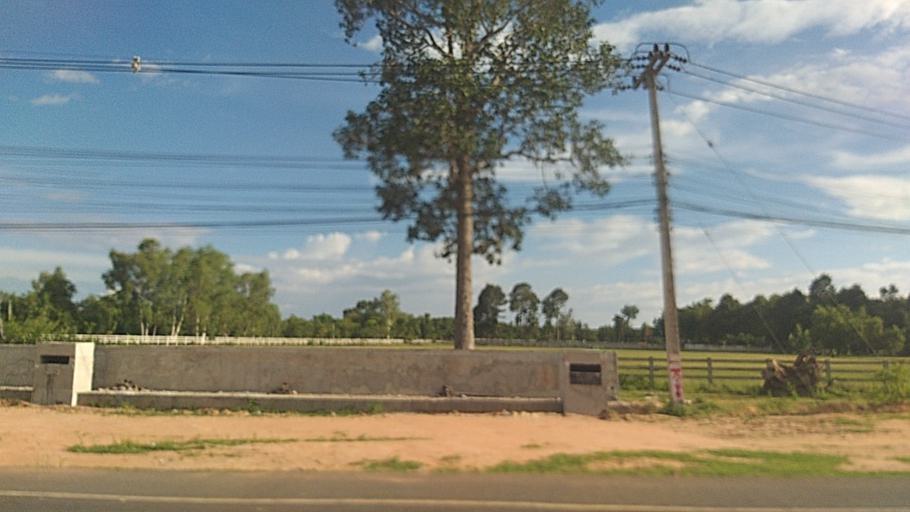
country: TH
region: Surin
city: Kap Choeng
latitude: 14.4773
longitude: 103.5896
